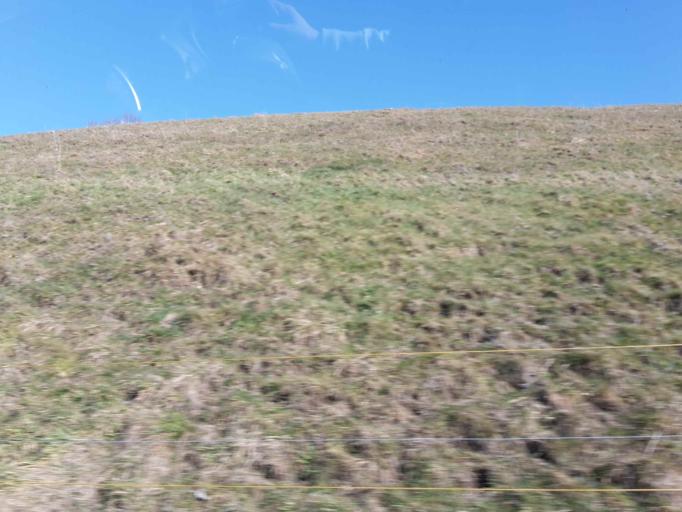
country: CH
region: Bern
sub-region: Emmental District
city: Durrenroth
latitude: 47.1020
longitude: 7.7770
